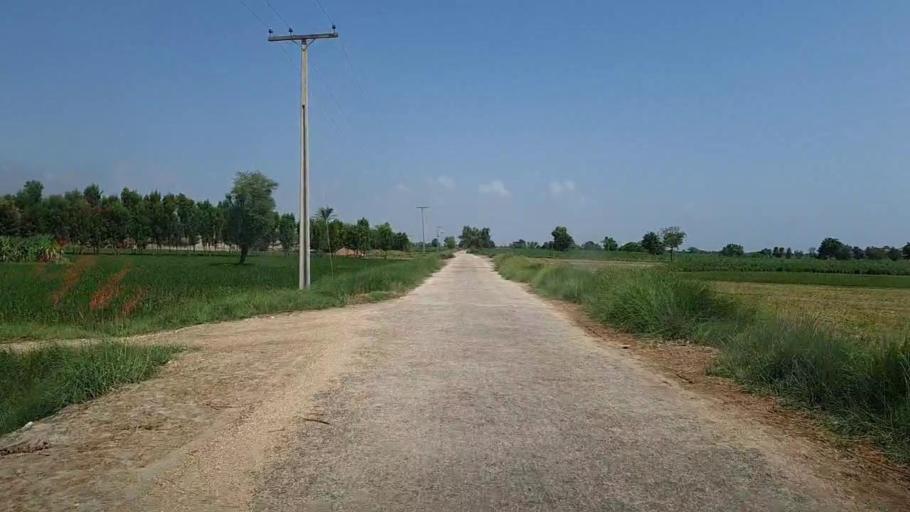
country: PK
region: Sindh
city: Bhiria
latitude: 26.8800
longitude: 68.2424
